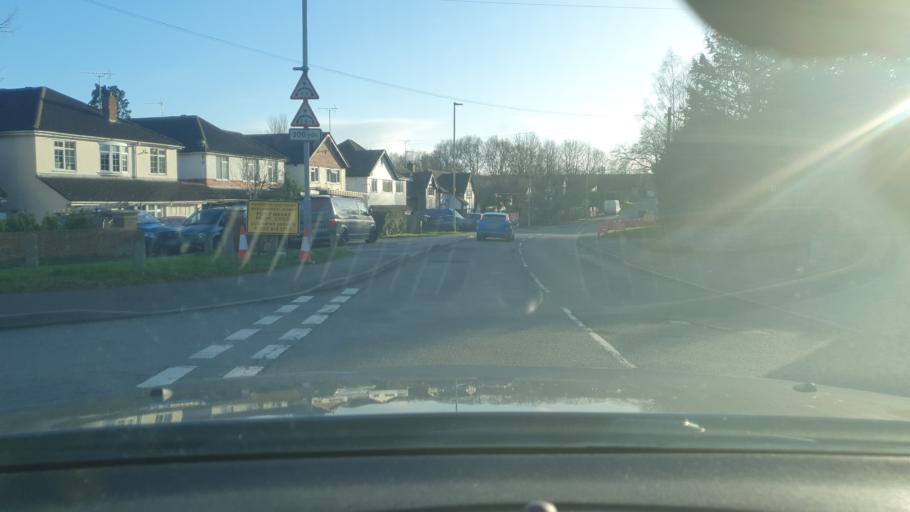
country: GB
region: England
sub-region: Wokingham
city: Woodley
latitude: 51.4408
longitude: -0.8978
